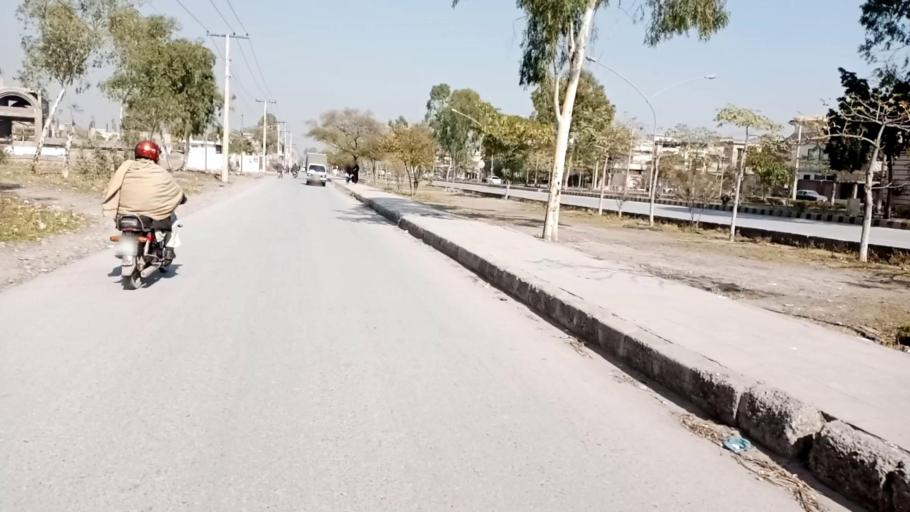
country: PK
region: Khyber Pakhtunkhwa
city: Peshawar
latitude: 33.9546
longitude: 71.4327
